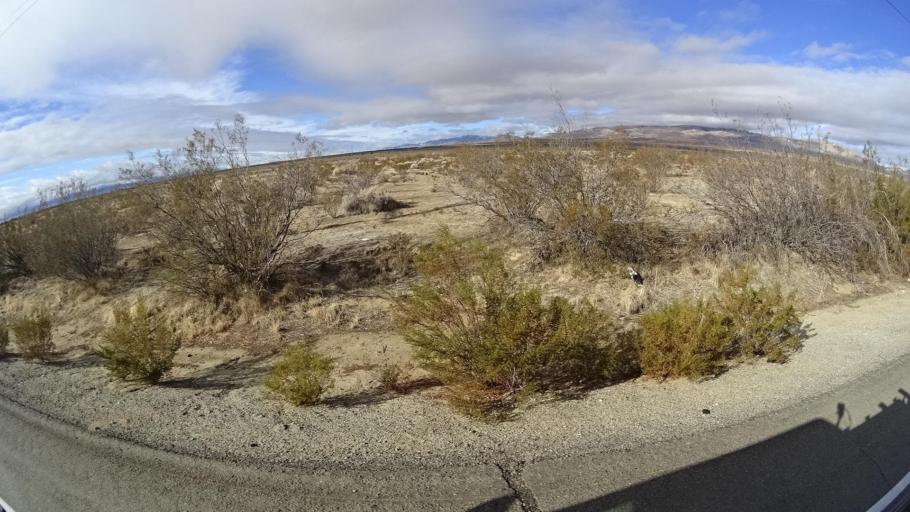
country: US
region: California
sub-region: Kern County
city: Rosamond
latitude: 34.9388
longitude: -118.2916
